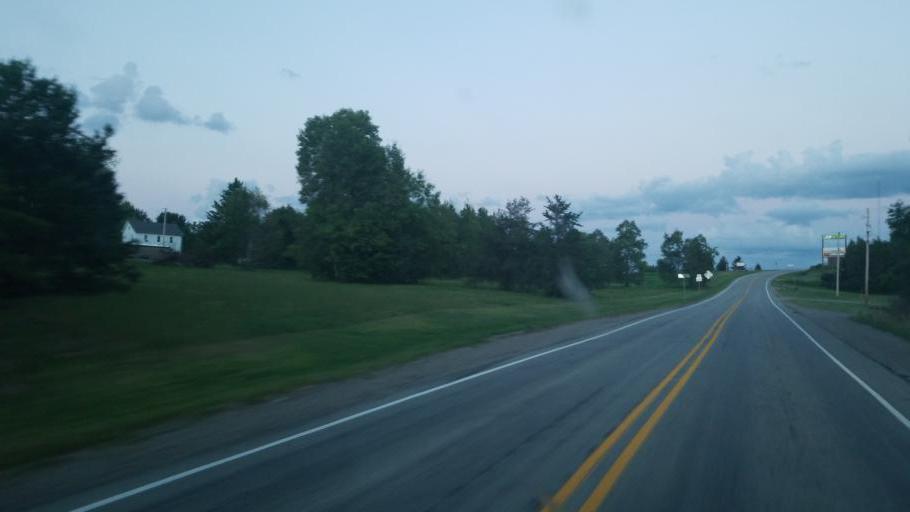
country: US
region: Pennsylvania
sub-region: Clarion County
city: Knox
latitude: 41.1912
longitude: -79.5475
